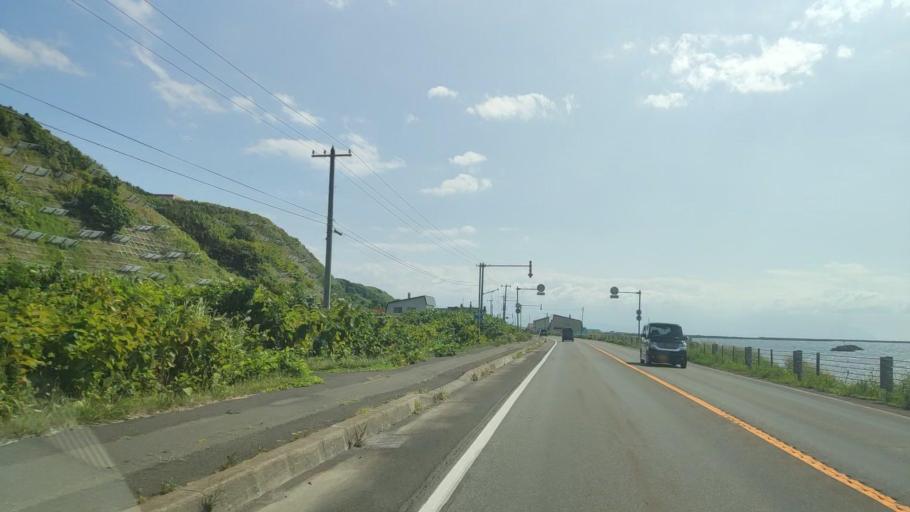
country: JP
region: Hokkaido
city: Rumoi
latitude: 43.9865
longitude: 141.6491
